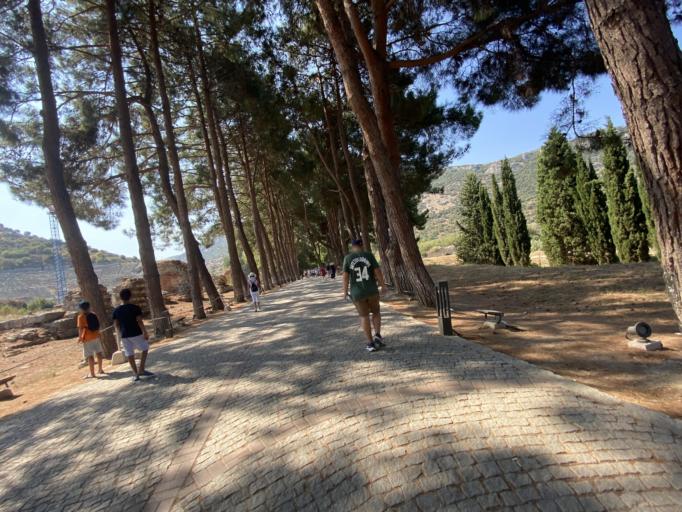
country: TR
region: Izmir
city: Selcuk
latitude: 37.9429
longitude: 27.3413
